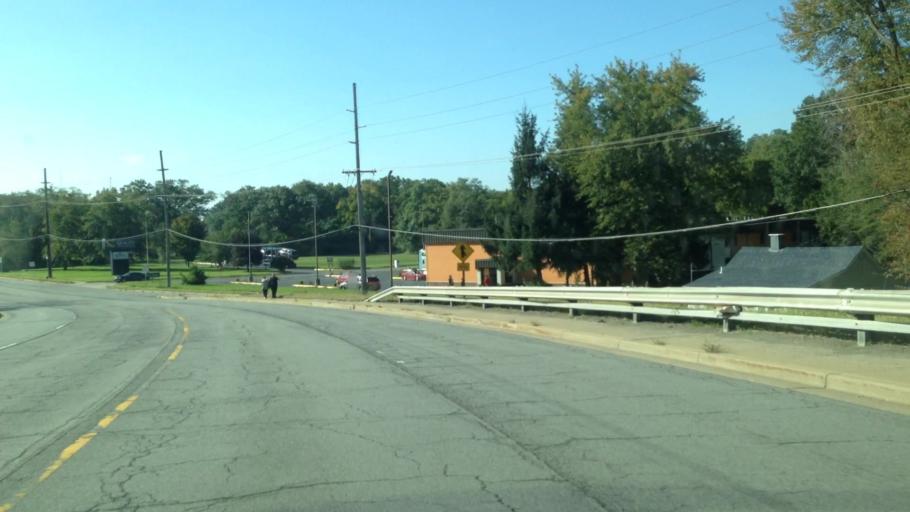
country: US
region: Indiana
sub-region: Porter County
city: Portage
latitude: 41.5861
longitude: -87.1830
